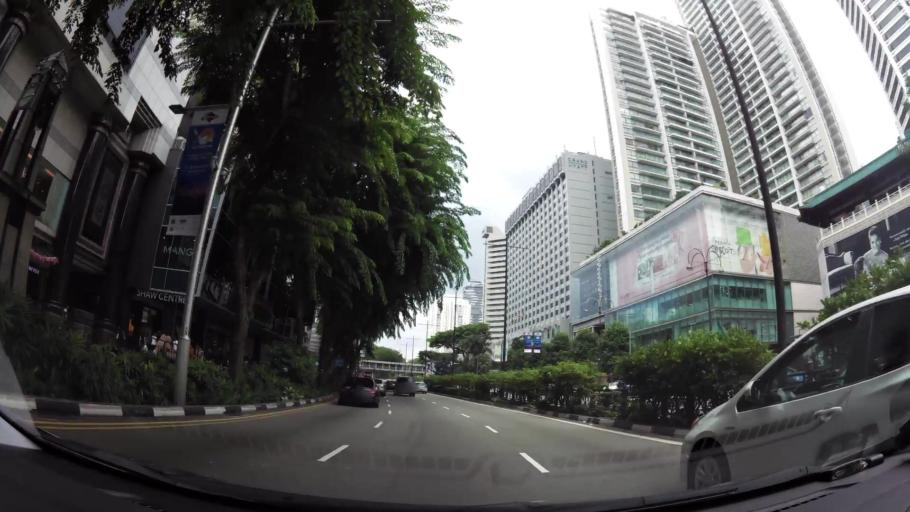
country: SG
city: Singapore
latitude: 1.3055
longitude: 103.8321
